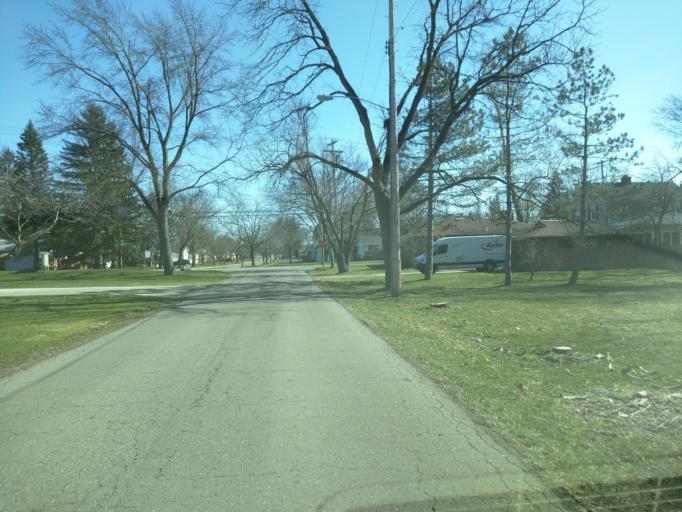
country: US
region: Michigan
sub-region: Ingham County
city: Edgemont Park
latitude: 42.7620
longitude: -84.5879
